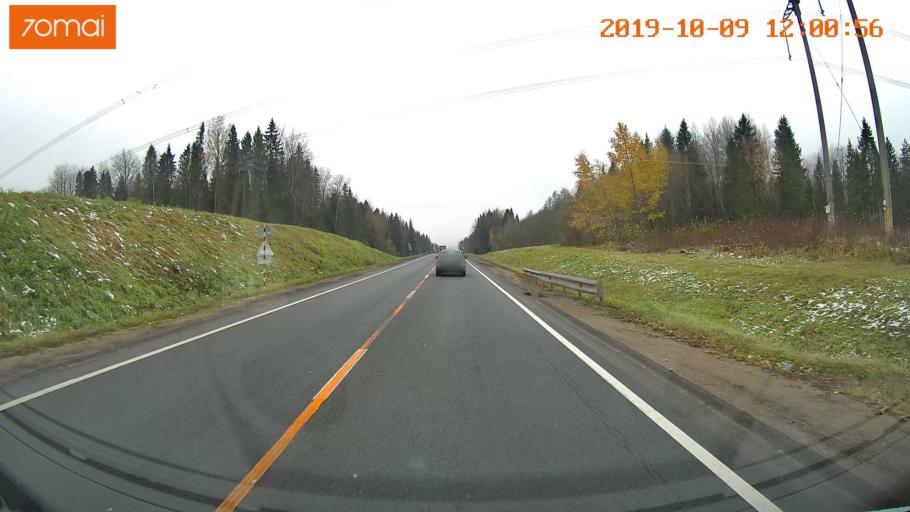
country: RU
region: Vologda
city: Gryazovets
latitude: 58.6933
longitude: 40.3012
